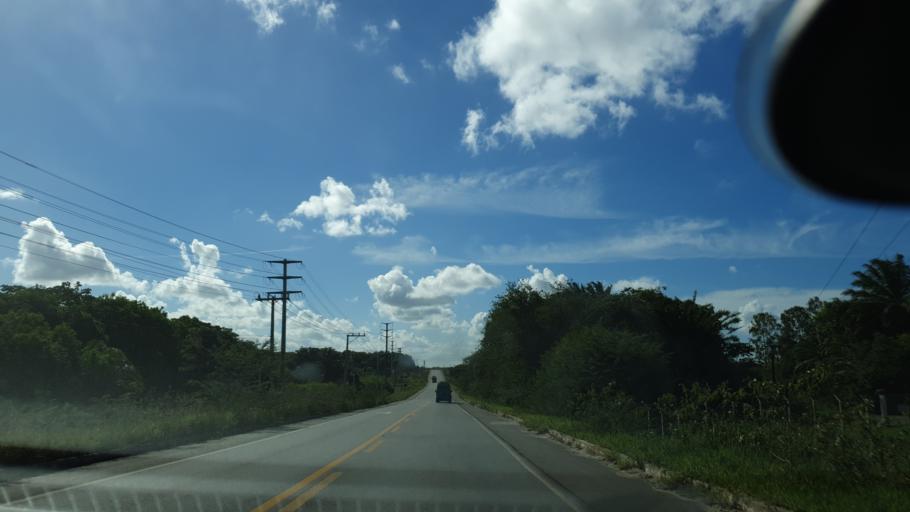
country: BR
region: Bahia
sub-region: Camacari
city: Camacari
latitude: -12.6835
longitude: -38.2339
